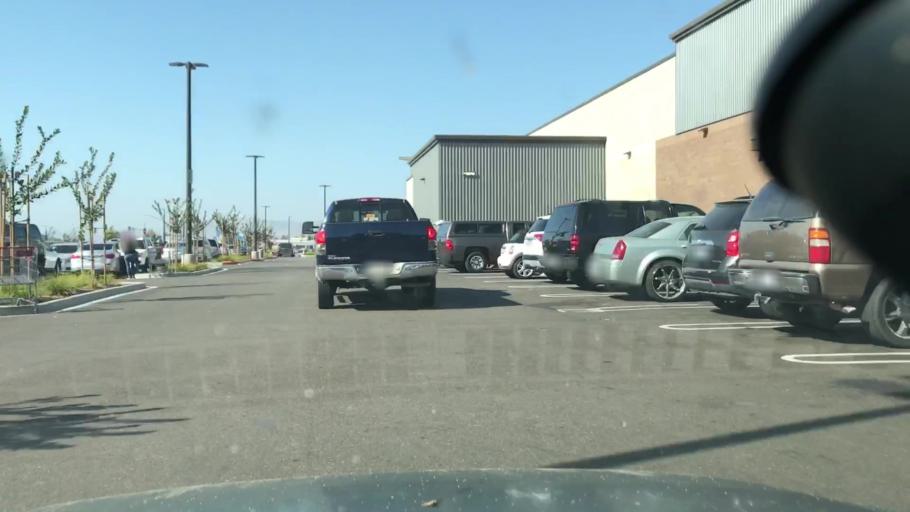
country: US
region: California
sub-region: Santa Barbara County
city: Santa Maria
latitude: 34.9261
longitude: -120.4197
